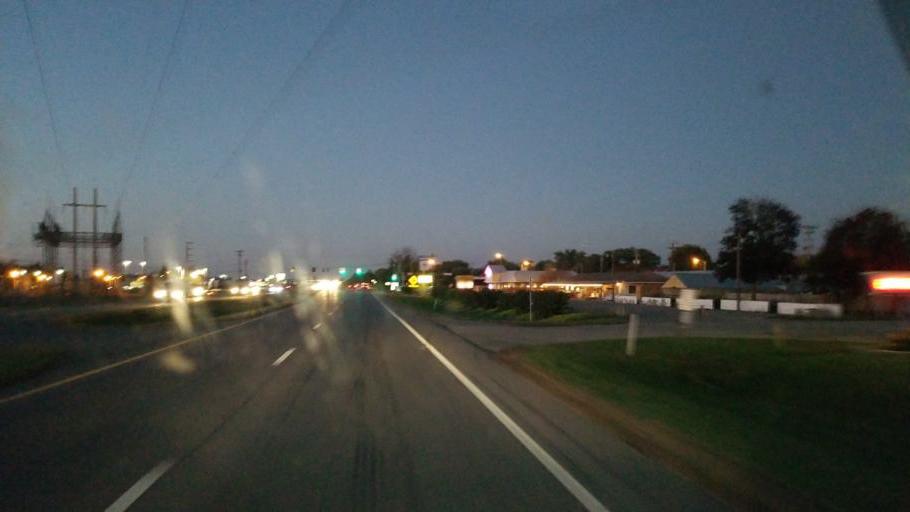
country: US
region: Ohio
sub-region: Pickaway County
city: Logan Elm Village
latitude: 39.5651
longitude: -82.9555
